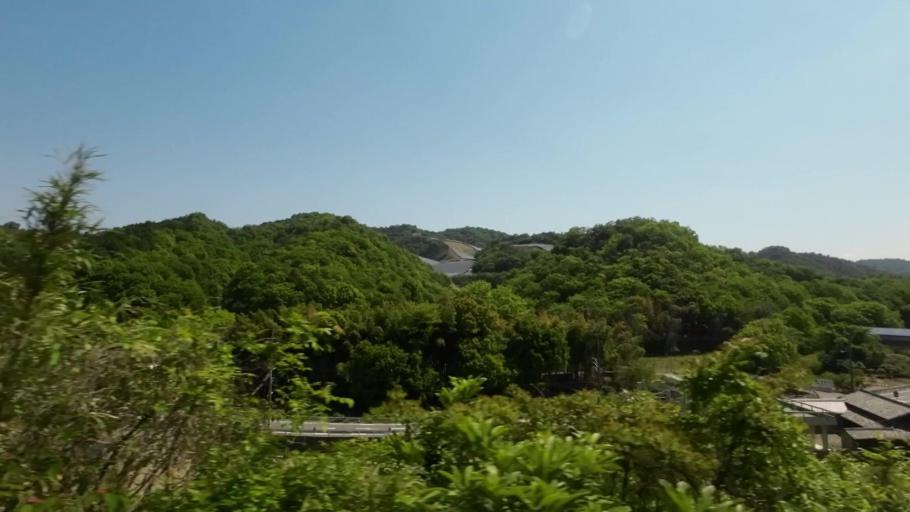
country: JP
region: Ehime
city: Niihama
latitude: 33.9674
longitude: 133.3589
